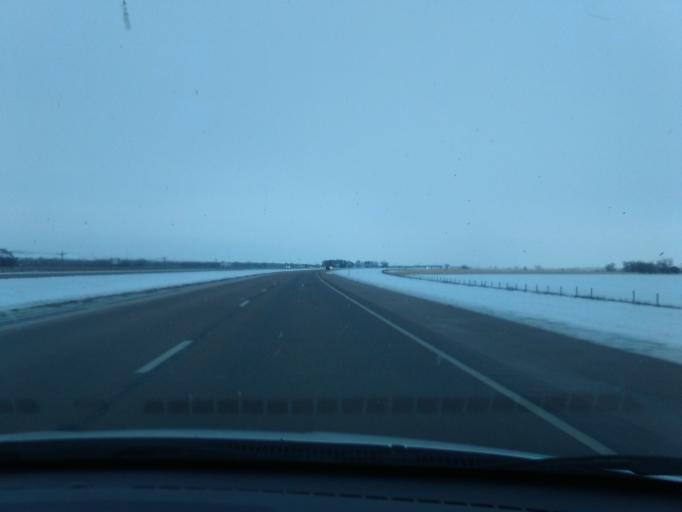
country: US
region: Nebraska
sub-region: Keith County
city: Ogallala
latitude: 41.1189
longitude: -101.6894
